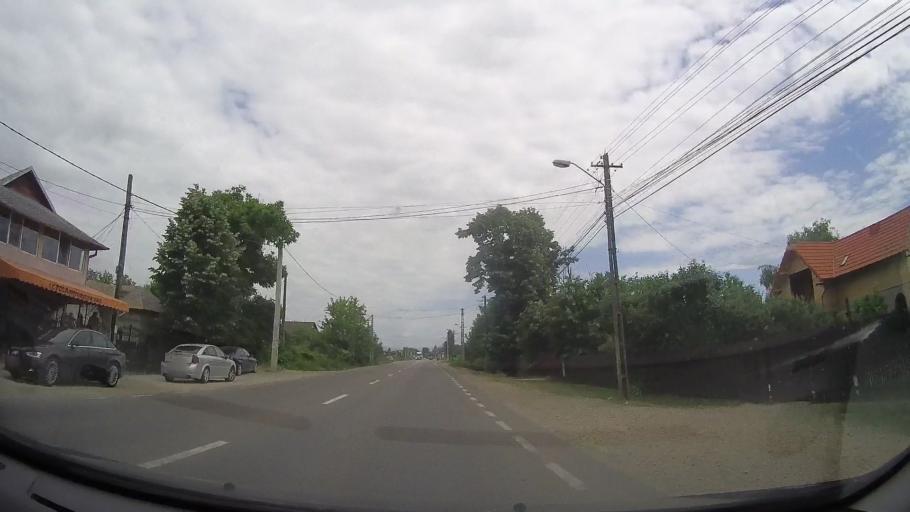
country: RO
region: Prahova
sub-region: Comuna Lipanesti
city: Sipotu
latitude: 45.0258
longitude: 26.0189
